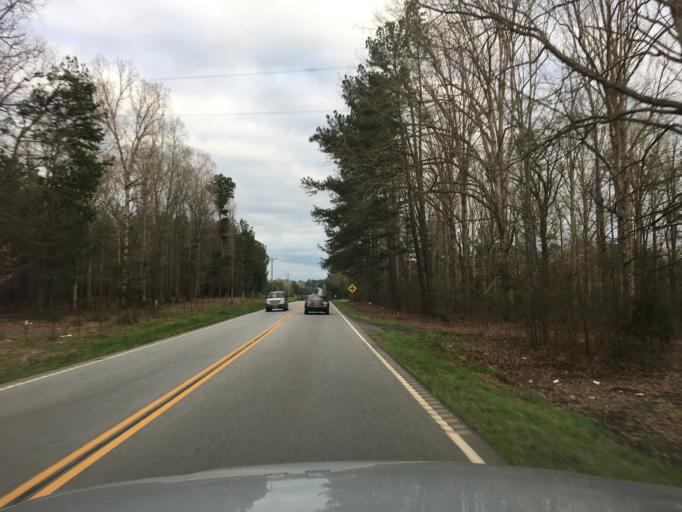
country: US
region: South Carolina
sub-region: Saluda County
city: Saluda
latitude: 34.0281
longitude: -81.7994
